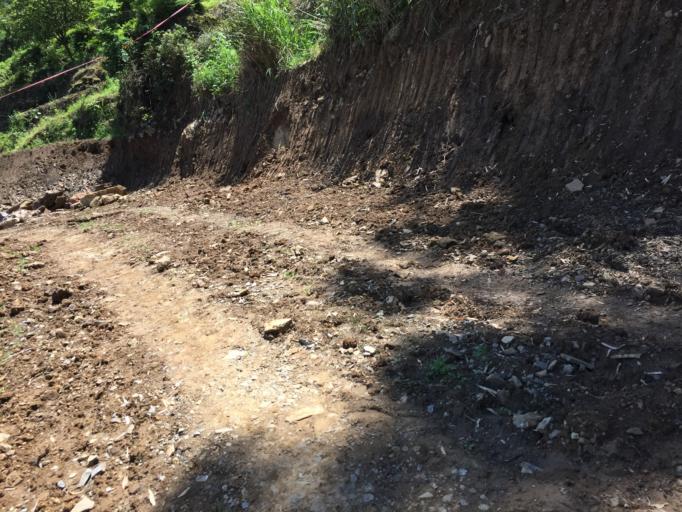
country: CN
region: Guizhou Sheng
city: Shiqian
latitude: 27.6740
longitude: 108.0836
